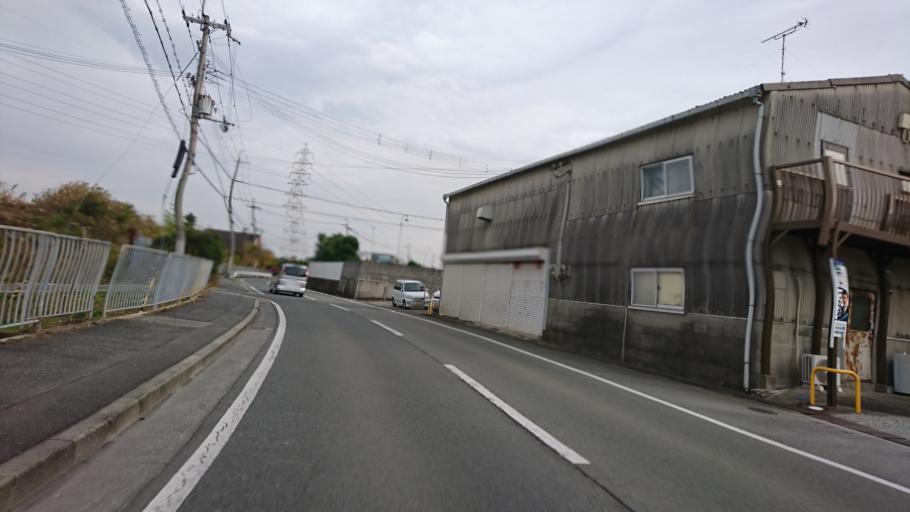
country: JP
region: Hyogo
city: Kakogawacho-honmachi
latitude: 34.7769
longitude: 134.8707
